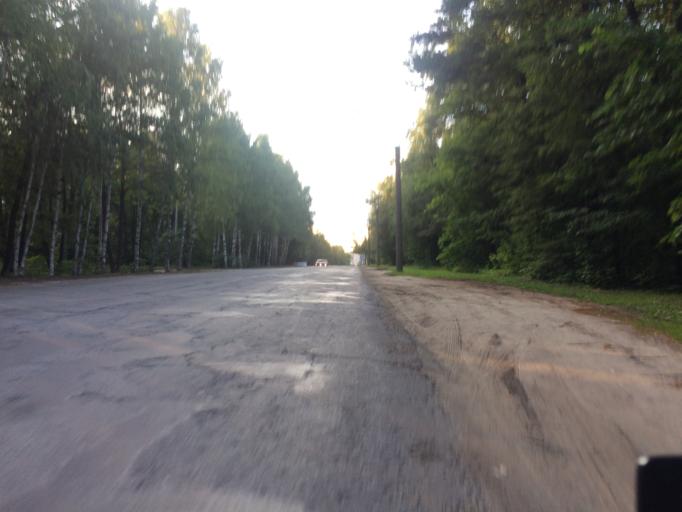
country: RU
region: Mariy-El
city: Yoshkar-Ola
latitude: 56.6242
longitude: 47.9542
